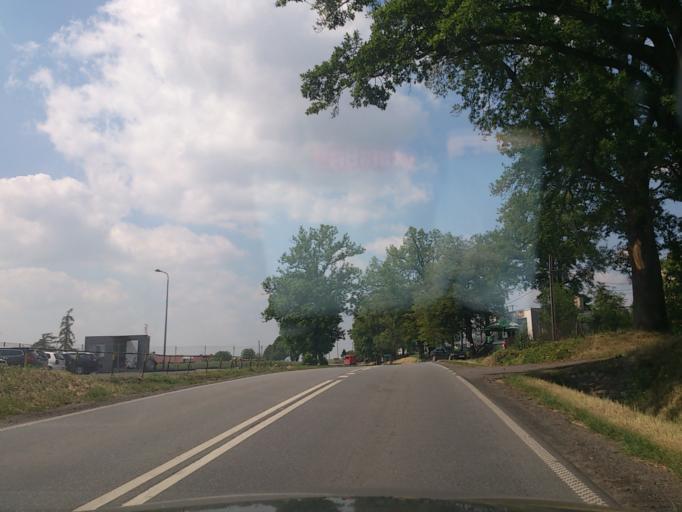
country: PL
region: Kujawsko-Pomorskie
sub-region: Powiat golubsko-dobrzynski
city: Radomin
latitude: 53.0950
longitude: 19.1554
